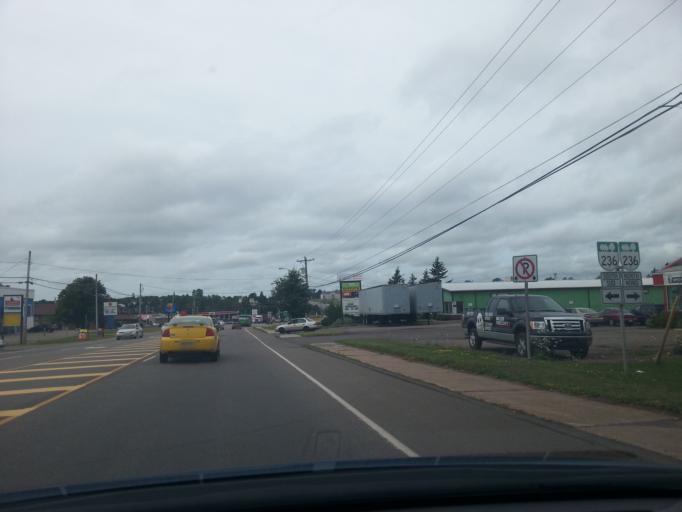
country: CA
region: Prince Edward Island
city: Charlottetown
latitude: 46.2651
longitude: -63.1542
